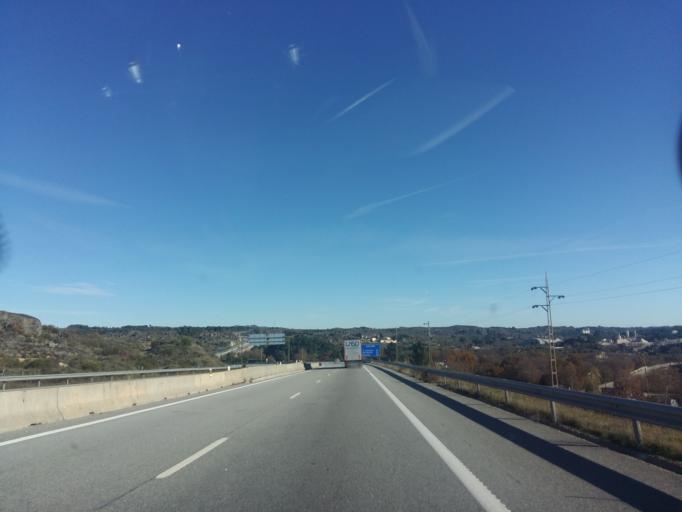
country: PT
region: Guarda
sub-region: Guarda
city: Sequeira
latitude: 40.5737
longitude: -7.1983
